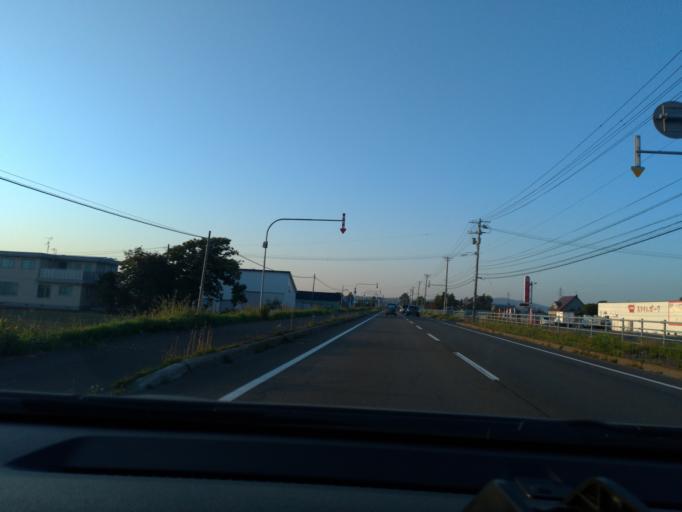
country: JP
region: Hokkaido
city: Tobetsu
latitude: 43.1949
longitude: 141.5235
